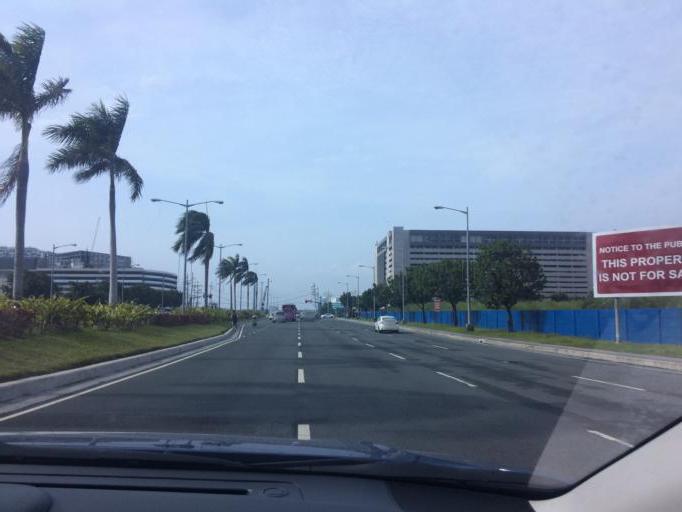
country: PH
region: Metro Manila
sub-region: Makati City
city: Makati City
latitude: 14.5264
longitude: 120.9850
